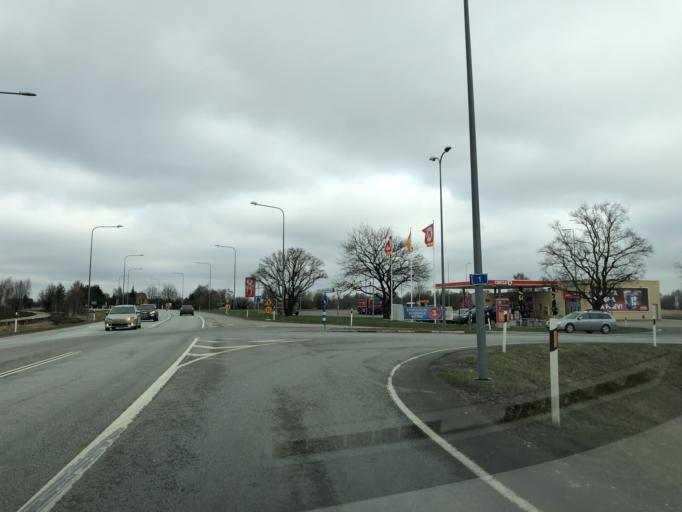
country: EE
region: Laeaene-Virumaa
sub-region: Rakvere linn
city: Rakvere
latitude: 59.3653
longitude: 26.3372
